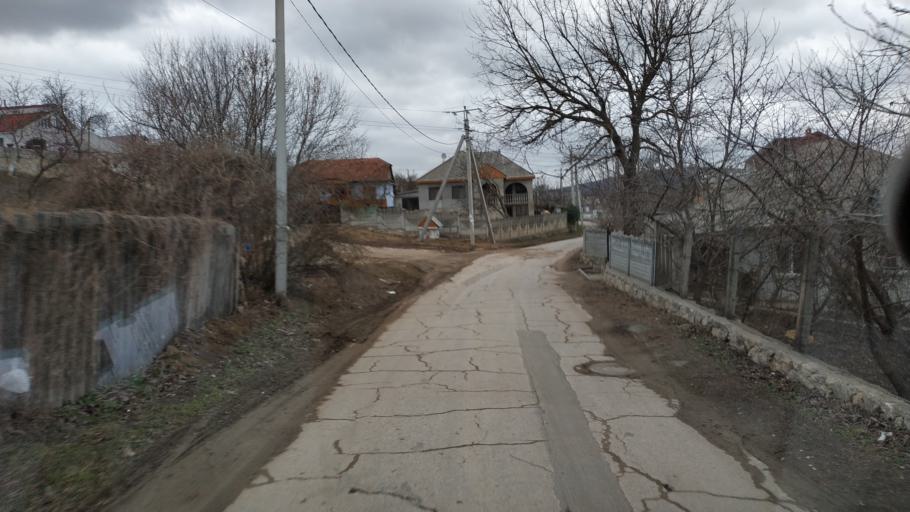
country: MD
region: Calarasi
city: Calarasi
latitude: 47.2422
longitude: 28.3079
